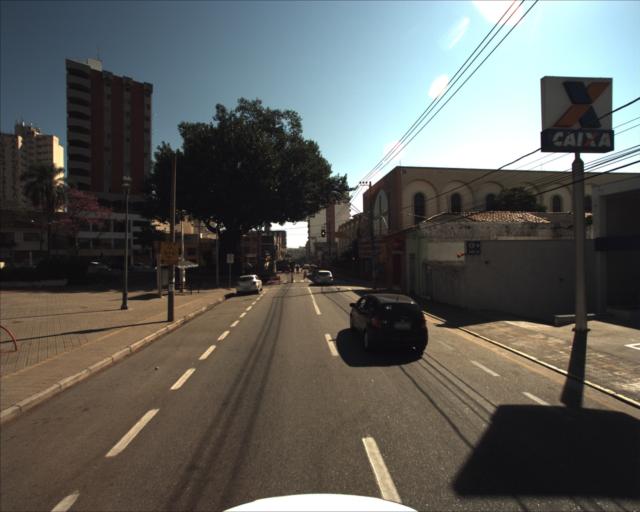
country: BR
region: Sao Paulo
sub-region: Sorocaba
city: Sorocaba
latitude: -23.4991
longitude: -47.4540
